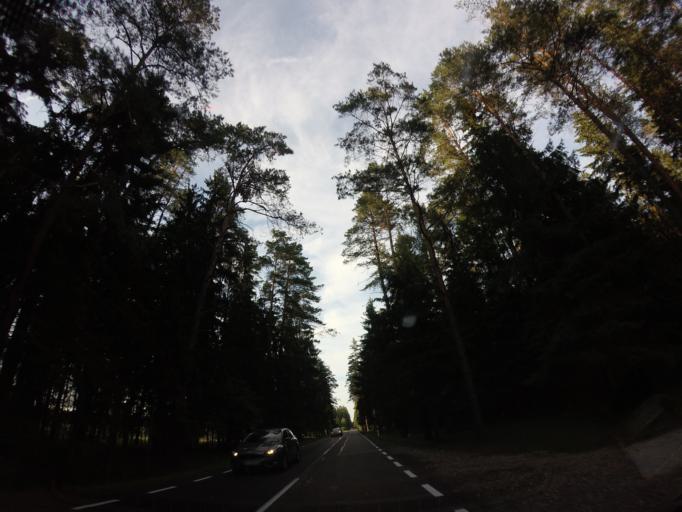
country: PL
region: Podlasie
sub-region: Powiat sejnenski
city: Krasnopol
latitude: 53.9297
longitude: 23.1620
